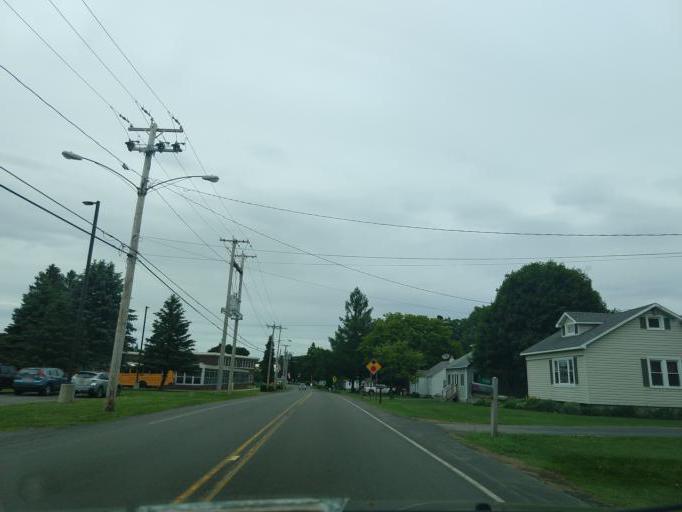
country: US
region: New York
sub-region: Cortland County
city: Munsons Corners
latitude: 42.5084
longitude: -76.1955
